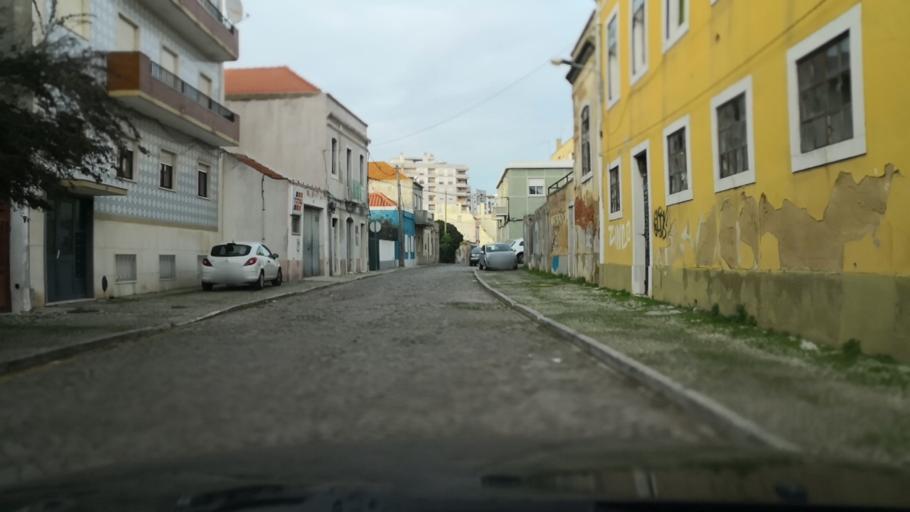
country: PT
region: Setubal
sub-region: Setubal
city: Setubal
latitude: 38.5254
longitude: -8.8826
